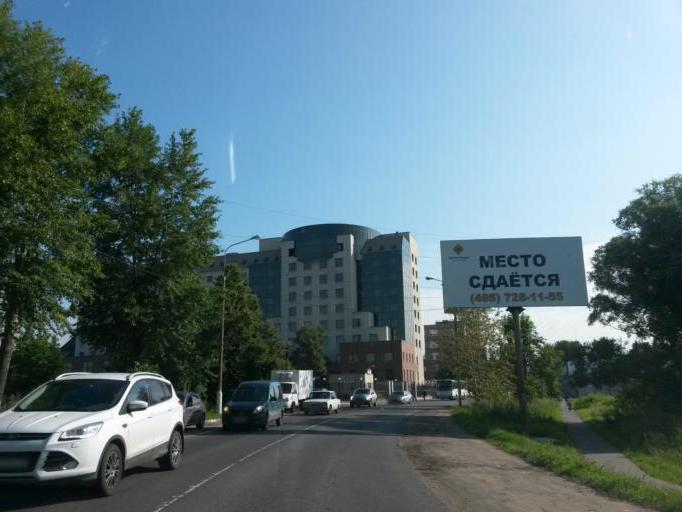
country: RU
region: Moskovskaya
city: Razvilka
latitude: 55.5908
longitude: 37.7351
